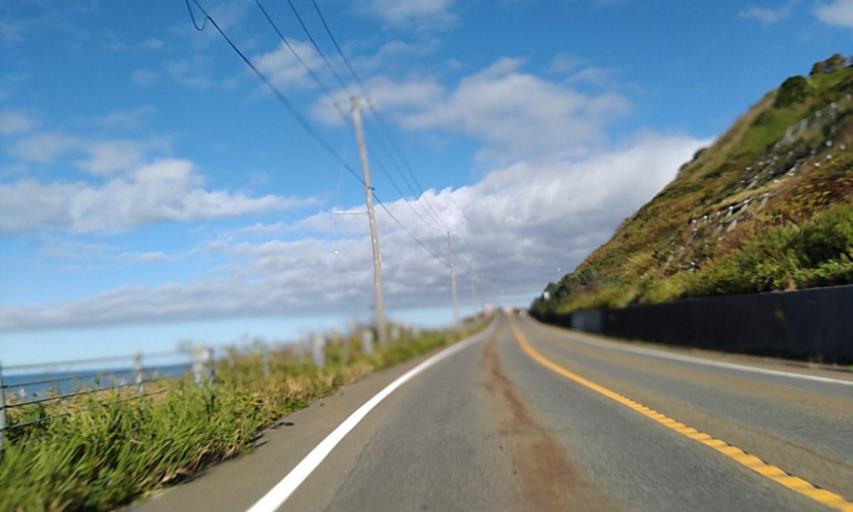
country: JP
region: Hokkaido
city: Shizunai-furukawacho
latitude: 42.2102
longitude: 142.6463
